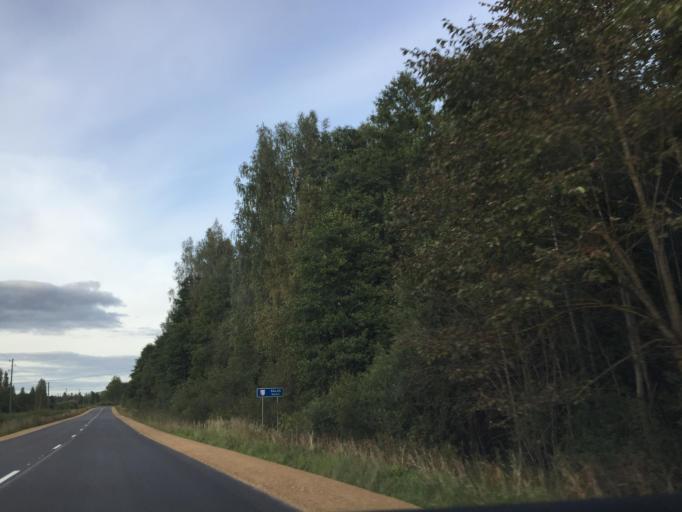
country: LV
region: Viesite
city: Viesite
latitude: 56.3851
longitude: 25.6705
